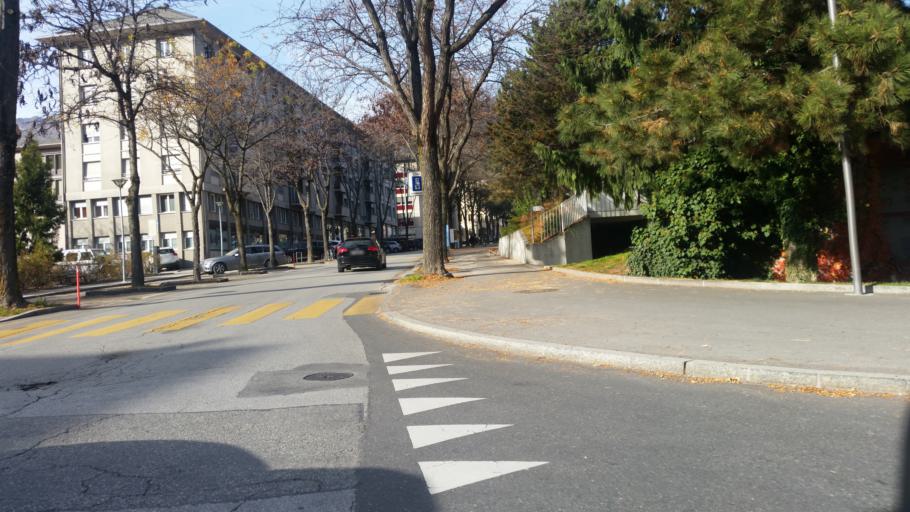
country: CH
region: Valais
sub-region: Sion District
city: Sitten
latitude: 46.2295
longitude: 7.3617
